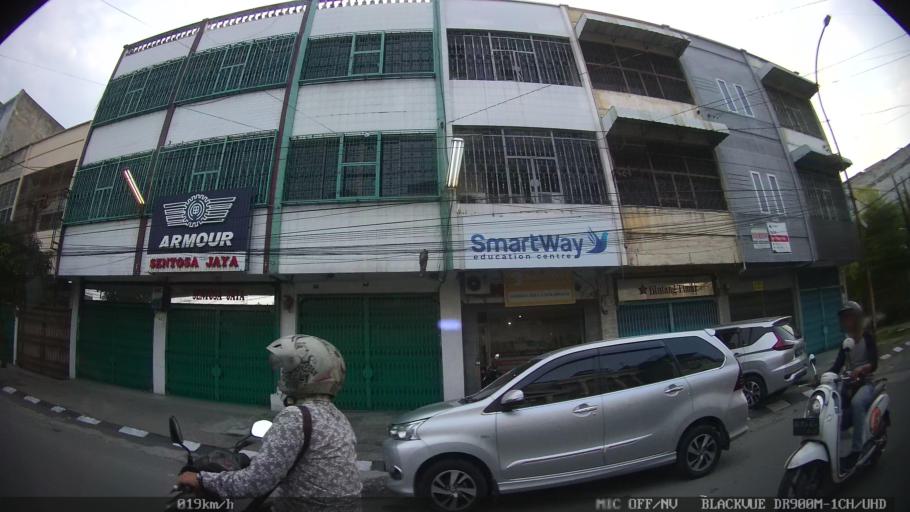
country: ID
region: North Sumatra
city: Medan
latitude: 3.5946
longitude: 98.6878
